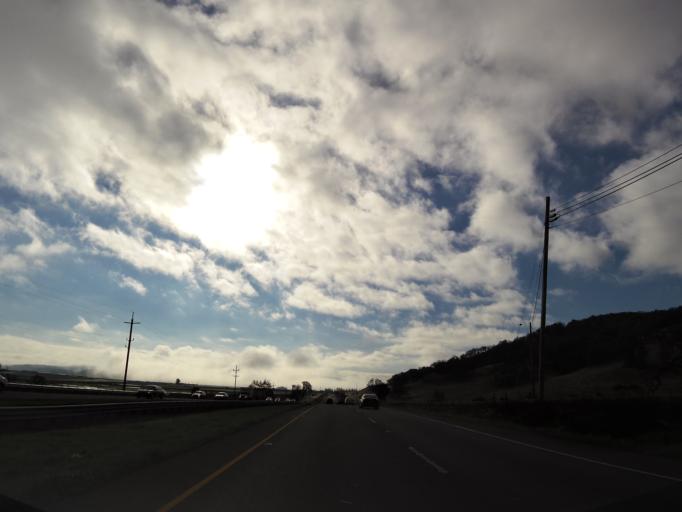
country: US
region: California
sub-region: Marin County
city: Novato
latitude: 38.1529
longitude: -122.5676
